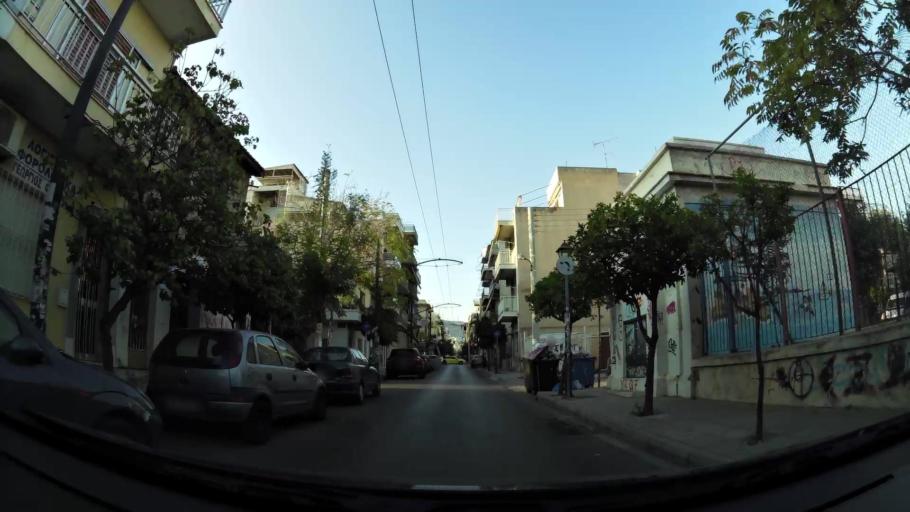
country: GR
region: Attica
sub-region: Nomos Piraios
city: Nikaia
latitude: 37.9679
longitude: 23.6469
